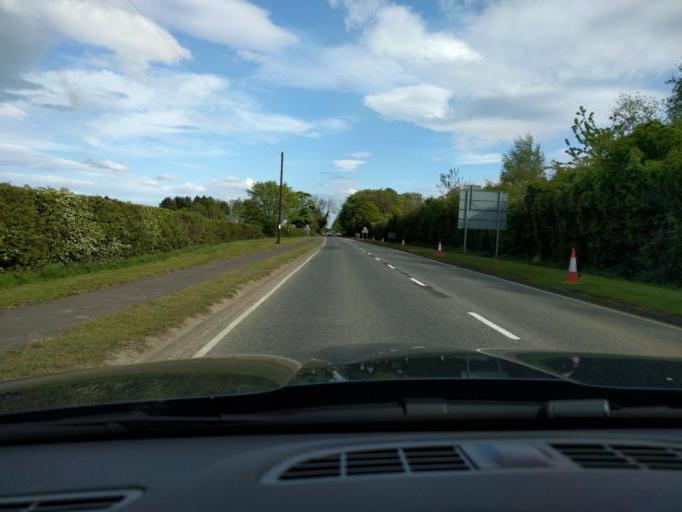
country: GB
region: England
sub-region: Northumberland
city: Morpeth
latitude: 55.1552
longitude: -1.6731
